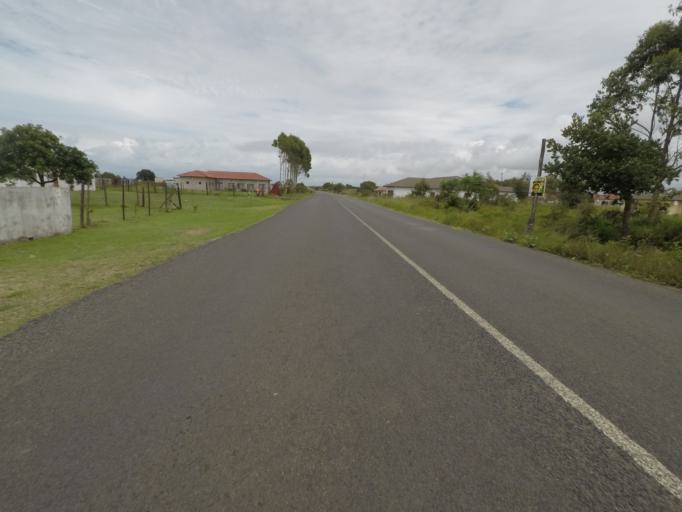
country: ZA
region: KwaZulu-Natal
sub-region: uThungulu District Municipality
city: eSikhawini
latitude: -28.9050
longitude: 31.8856
